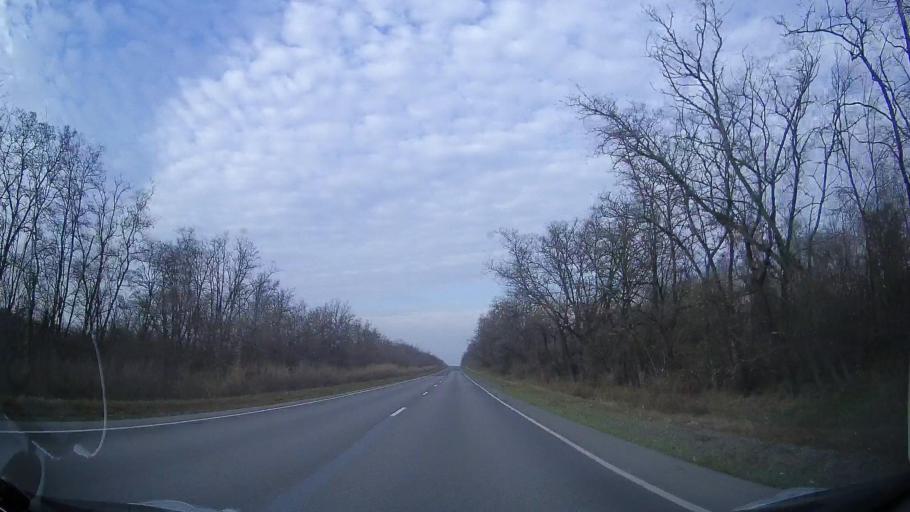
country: RU
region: Rostov
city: Bagayevskaya
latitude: 47.1192
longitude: 40.2767
